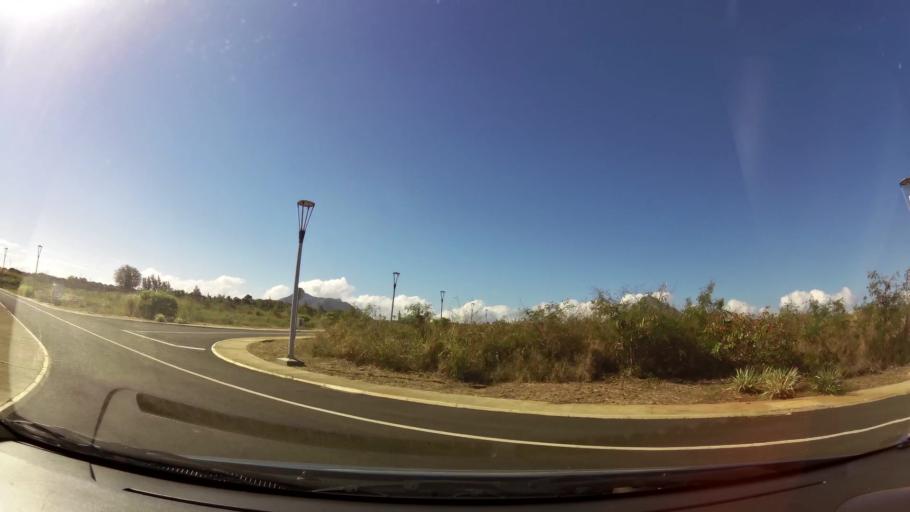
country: MU
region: Black River
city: Flic en Flac
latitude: -20.2677
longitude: 57.3795
